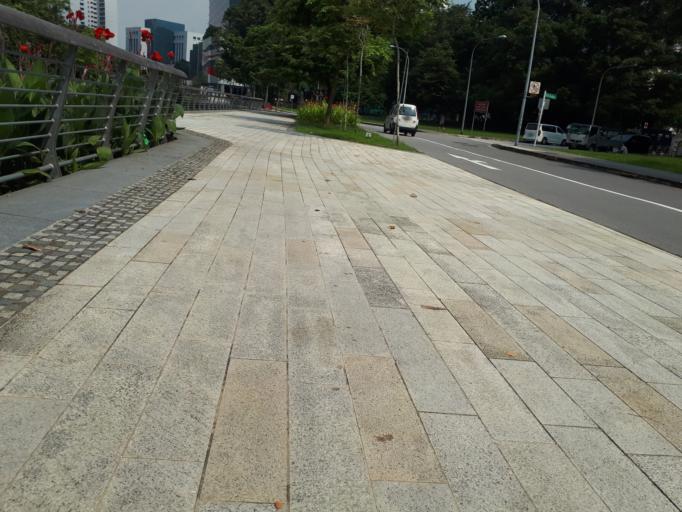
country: SG
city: Singapore
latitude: 1.3056
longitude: 103.8580
